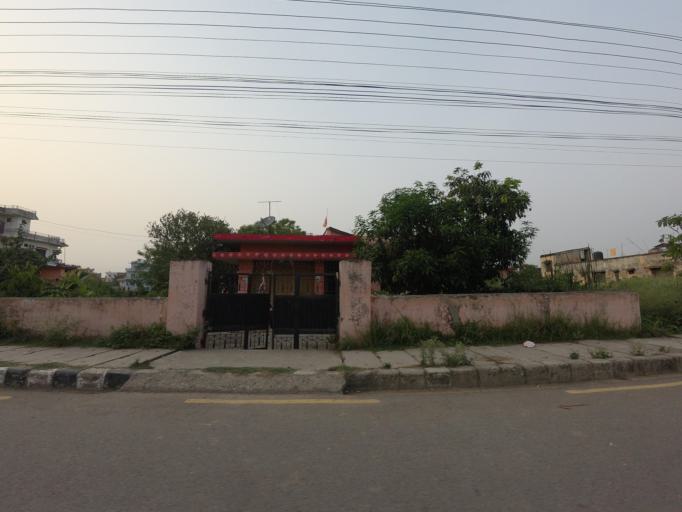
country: NP
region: Western Region
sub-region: Lumbini Zone
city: Bhairahawa
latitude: 27.5112
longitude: 83.4616
